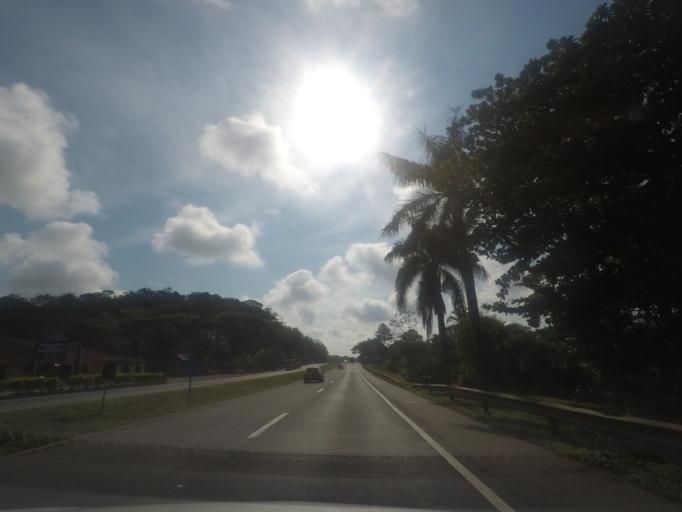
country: BR
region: Parana
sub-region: Antonina
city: Antonina
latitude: -25.5580
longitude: -48.8054
